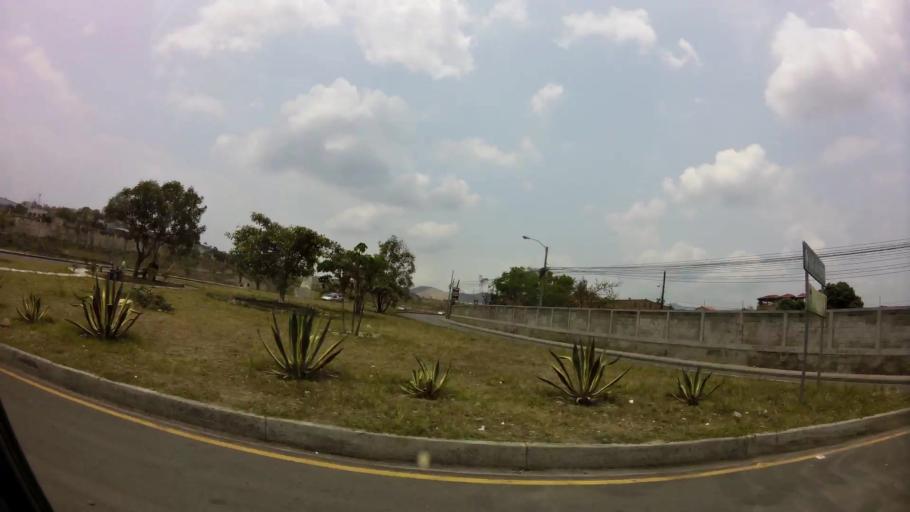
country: HN
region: Francisco Morazan
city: Tegucigalpa
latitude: 14.0526
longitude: -87.2210
